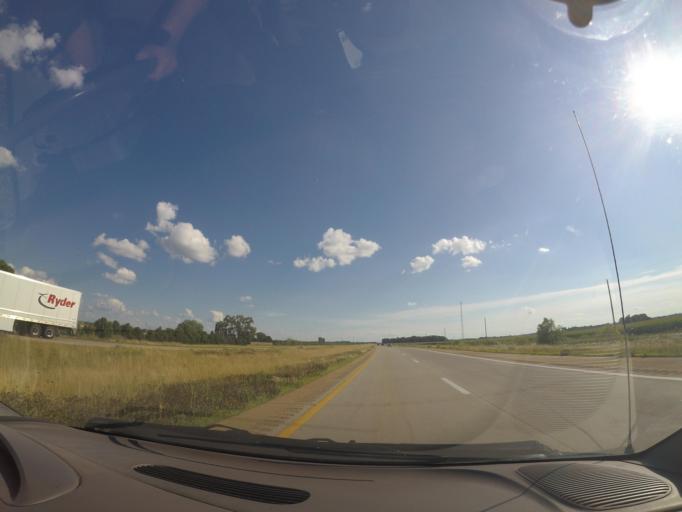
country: US
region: Ohio
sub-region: Lucas County
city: Whitehouse
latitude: 41.4930
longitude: -83.7675
